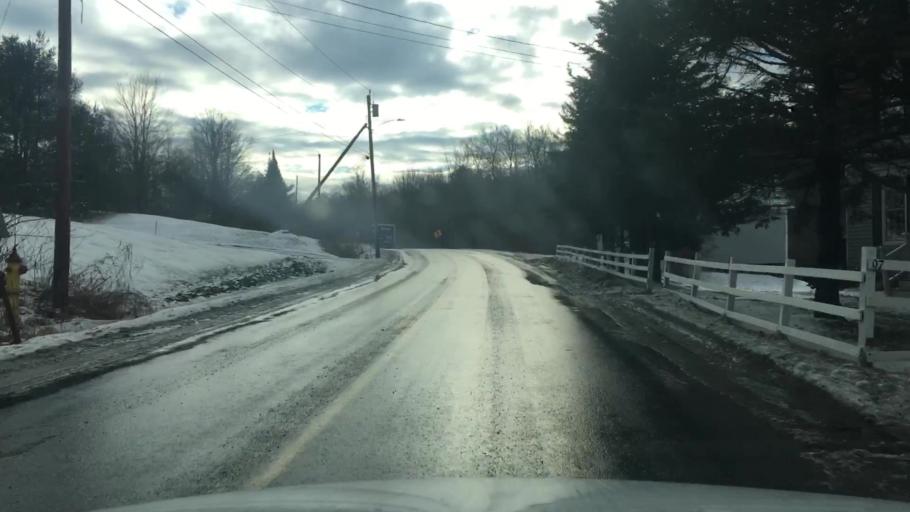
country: US
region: Maine
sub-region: Penobscot County
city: Brewer
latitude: 44.7624
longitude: -68.7756
